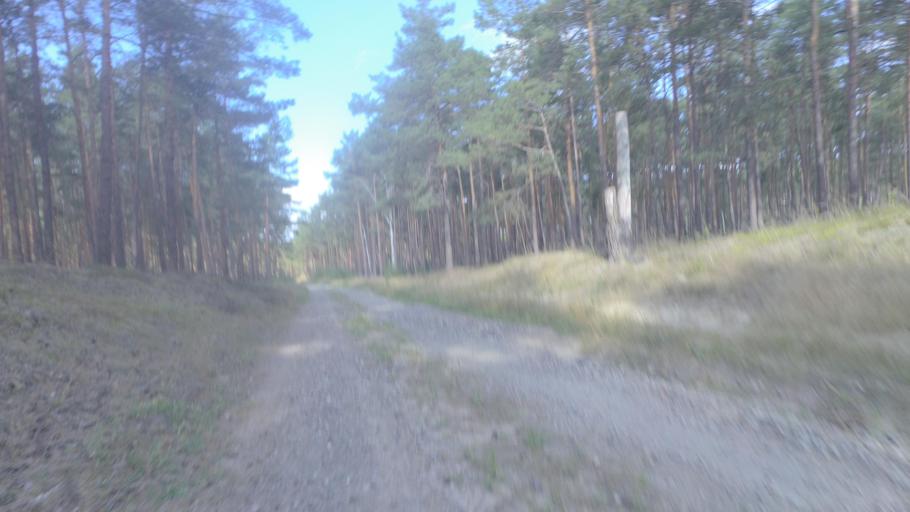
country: DE
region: Brandenburg
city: Munchehofe
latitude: 52.1818
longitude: 13.8720
